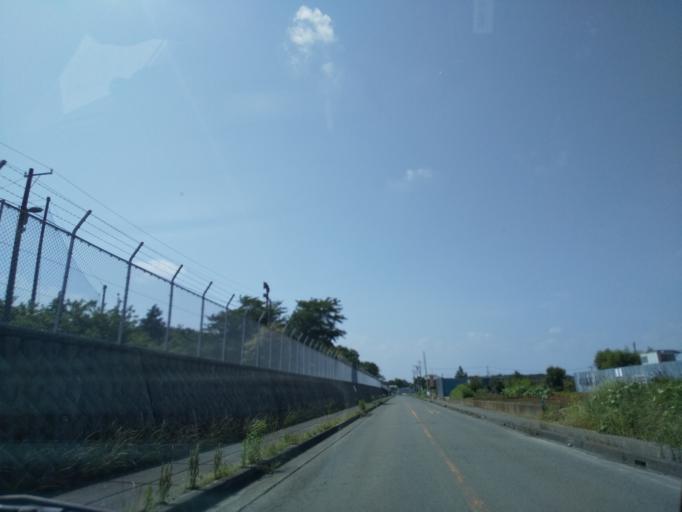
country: JP
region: Kanagawa
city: Zama
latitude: 35.5142
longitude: 139.3970
